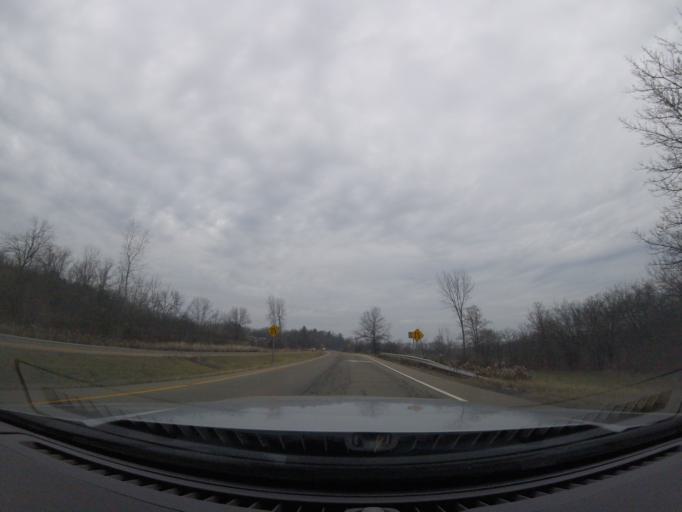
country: US
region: New York
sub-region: Schuyler County
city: Watkins Glen
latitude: 42.4223
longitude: -76.9041
